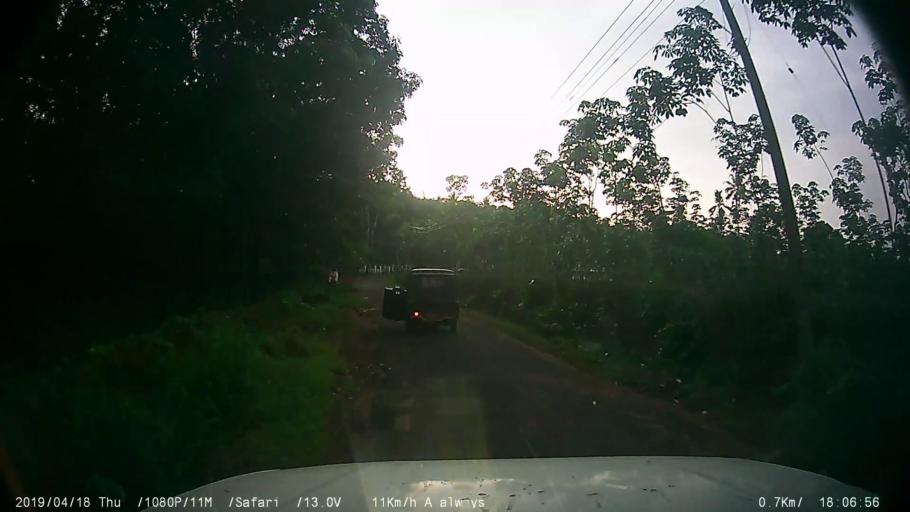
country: IN
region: Kerala
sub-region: Kottayam
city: Palackattumala
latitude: 9.7783
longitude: 76.5875
